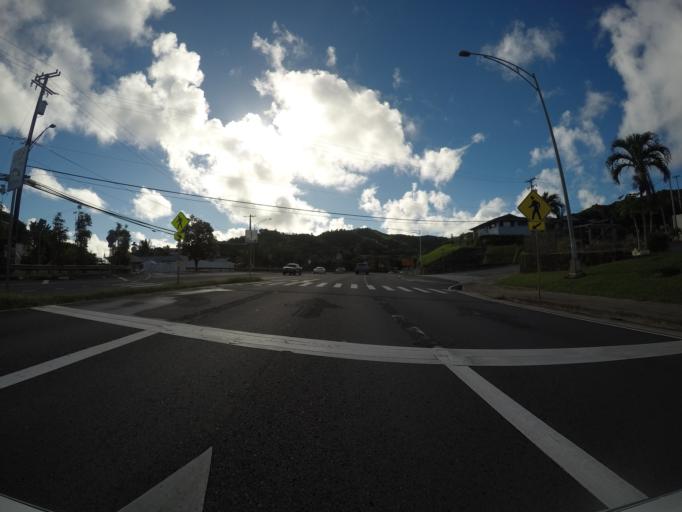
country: US
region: Hawaii
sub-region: Honolulu County
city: Kane'ohe
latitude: 21.4110
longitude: -157.7743
